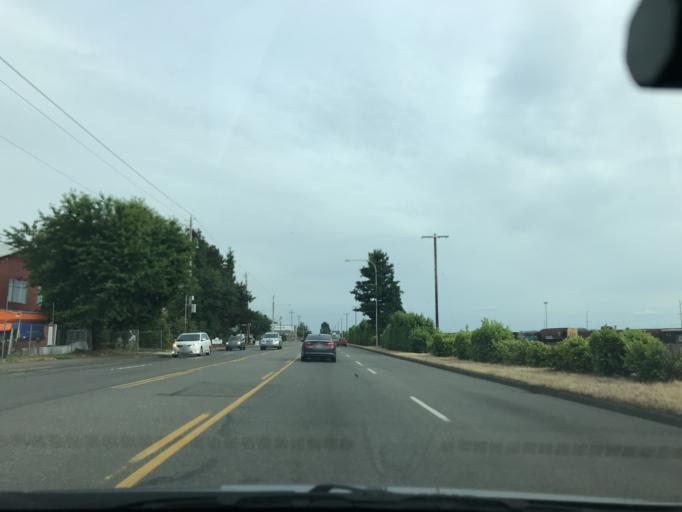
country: US
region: Washington
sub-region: King County
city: Auburn
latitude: 47.2885
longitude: -122.2290
